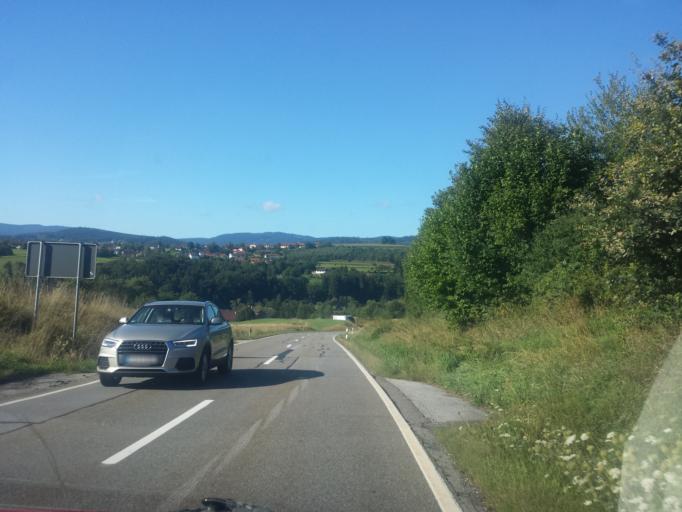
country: DE
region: Bavaria
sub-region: Lower Bavaria
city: Viechtach
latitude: 49.0962
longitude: 12.8860
